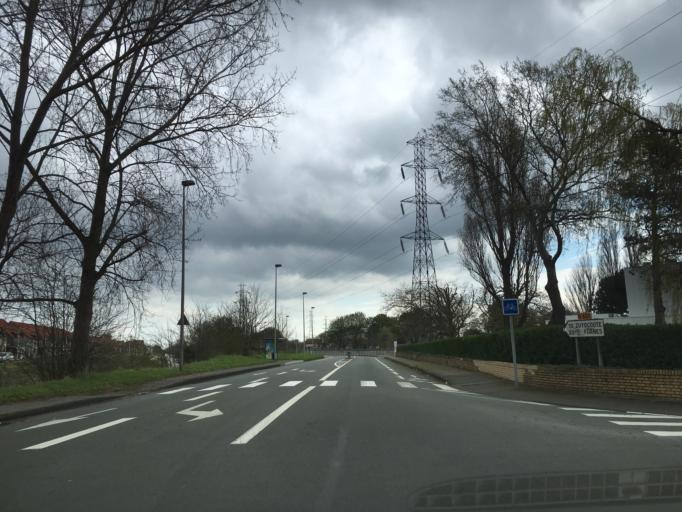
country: FR
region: Nord-Pas-de-Calais
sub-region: Departement du Nord
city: Dunkerque
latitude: 51.0298
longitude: 2.3845
